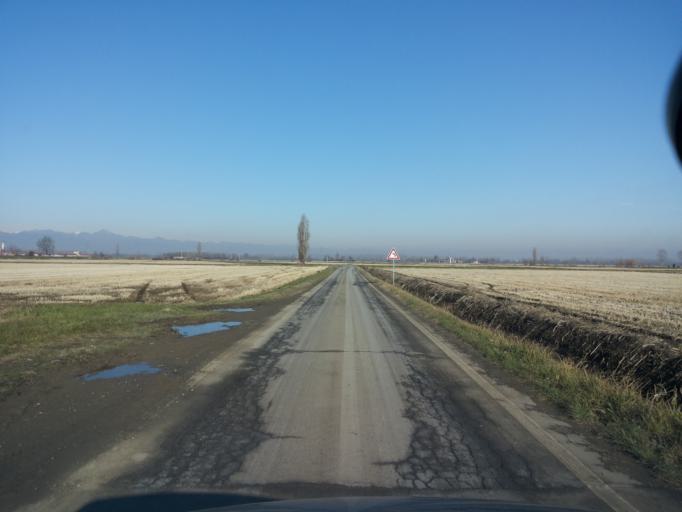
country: IT
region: Piedmont
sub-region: Provincia di Vercelli
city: San Germano Vercellese
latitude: 45.3817
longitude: 8.2446
